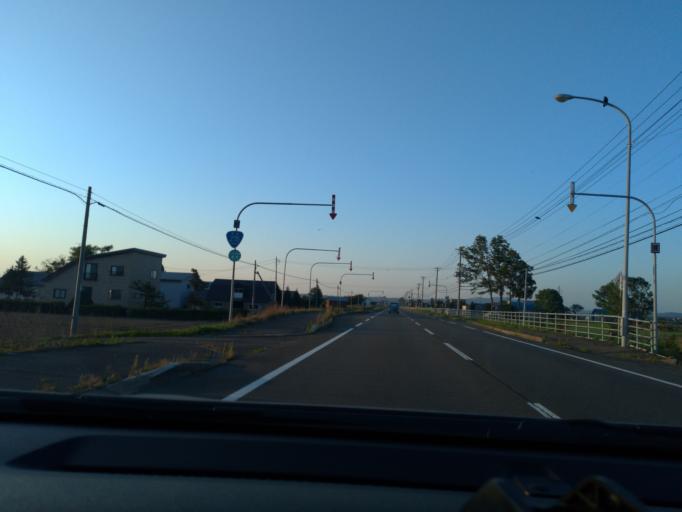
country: JP
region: Hokkaido
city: Tobetsu
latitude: 43.1923
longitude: 141.5244
